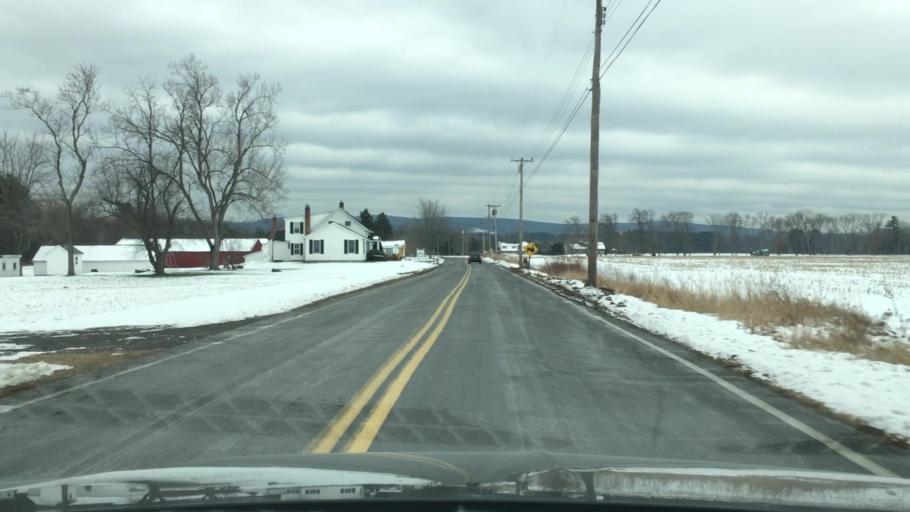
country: US
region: Connecticut
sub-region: Tolland County
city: Somers
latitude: 41.9999
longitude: -72.4741
